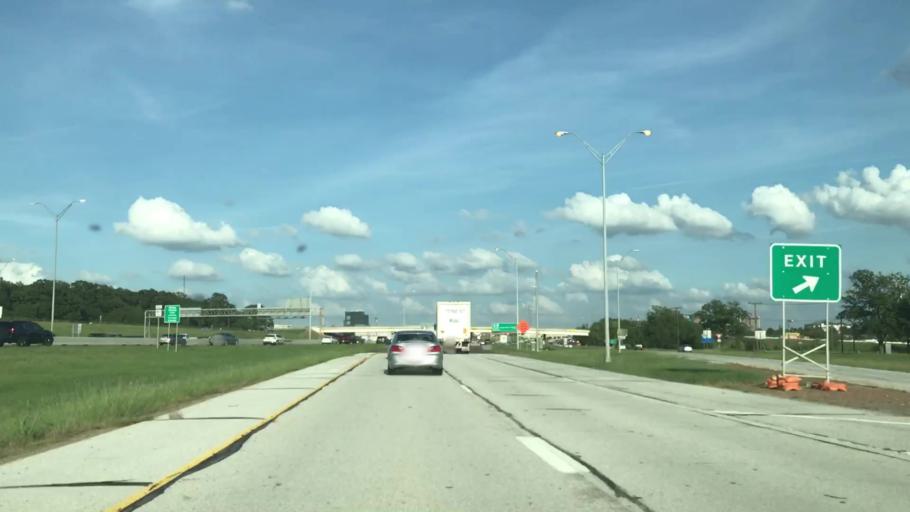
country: US
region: Texas
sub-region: Tarrant County
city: Euless
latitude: 32.8364
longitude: -97.0341
